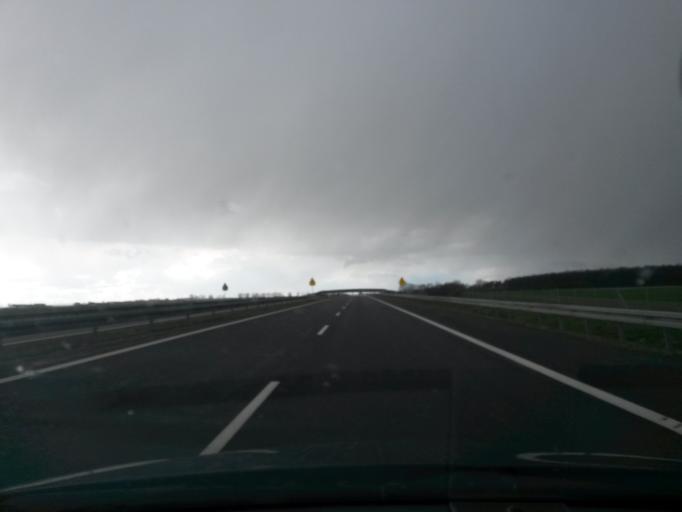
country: PL
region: Greater Poland Voivodeship
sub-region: Powiat sredzki
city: Sroda Wielkopolska
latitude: 52.3102
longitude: 17.2534
